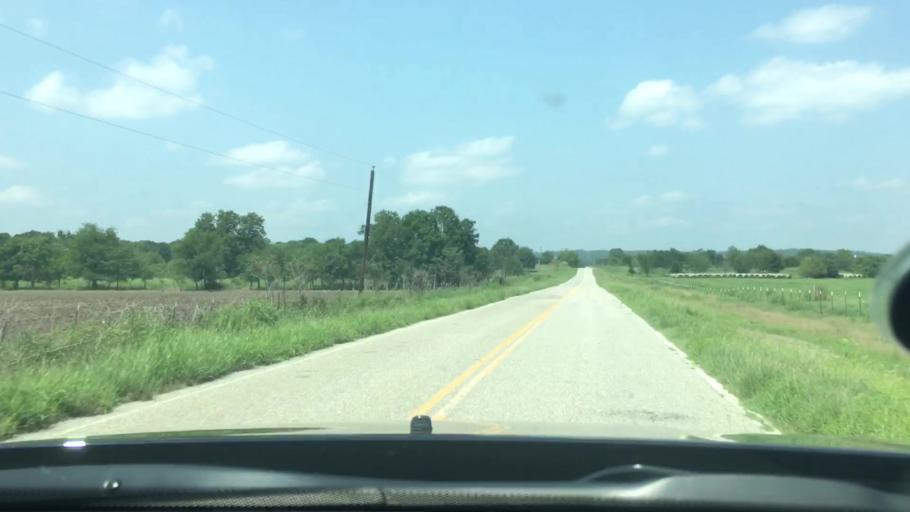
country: US
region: Oklahoma
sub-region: Johnston County
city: Tishomingo
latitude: 34.3930
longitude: -96.4962
